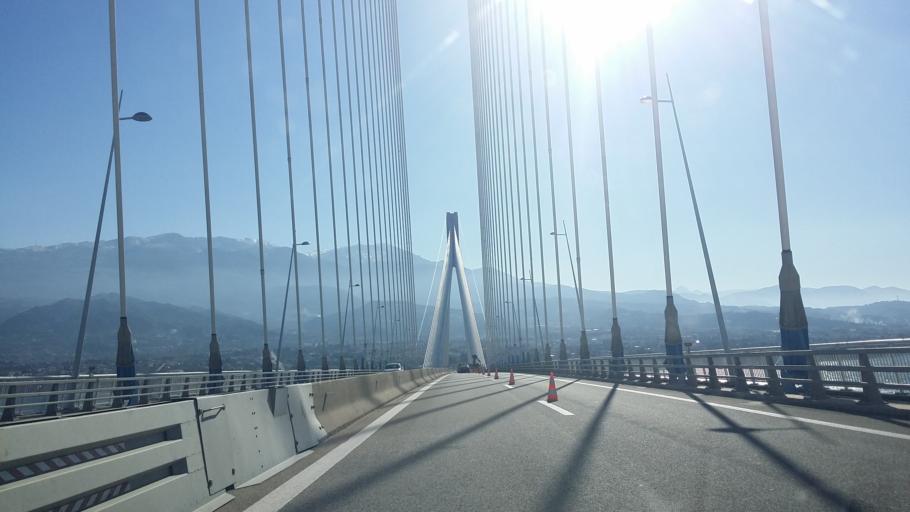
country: GR
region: West Greece
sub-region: Nomos Aitolias kai Akarnanias
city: Antirrio
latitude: 38.3182
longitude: 21.7744
